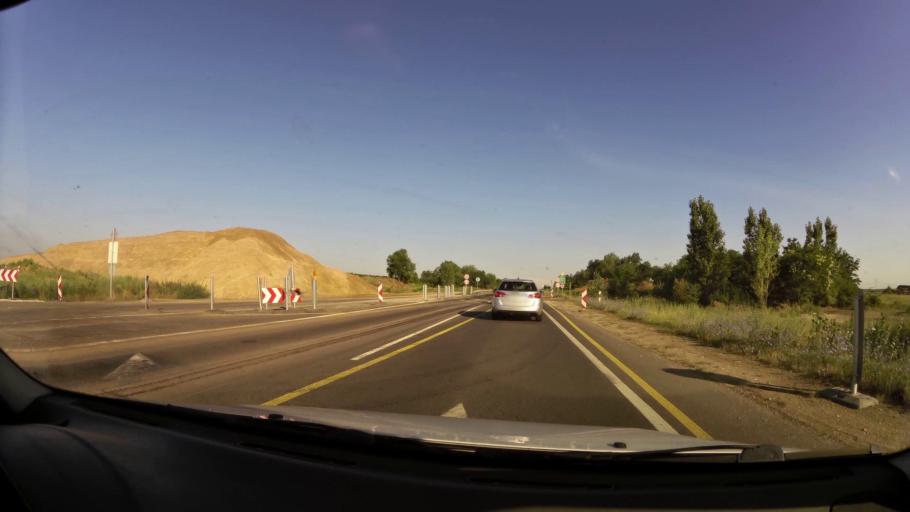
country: HU
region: Pest
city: Cegledbercel
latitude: 47.2218
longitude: 19.6951
